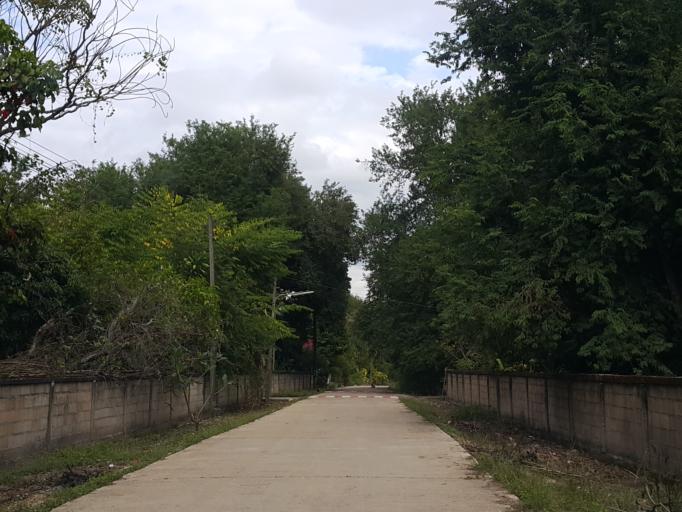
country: TH
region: Lampang
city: Chae Hom
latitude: 18.6410
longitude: 99.5400
